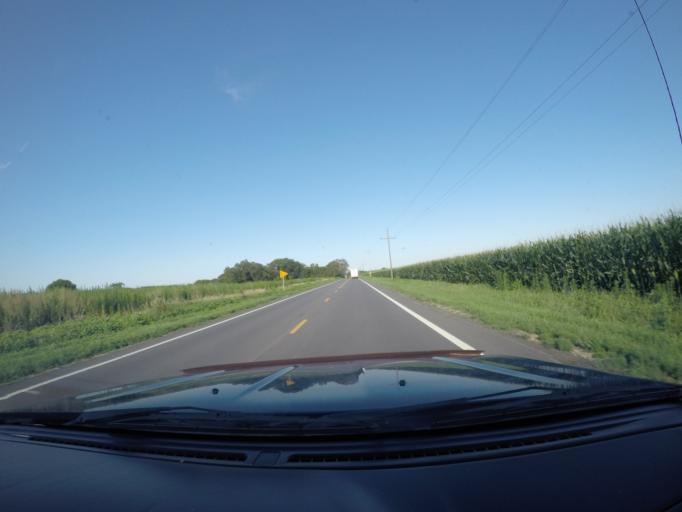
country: US
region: Kansas
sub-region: Douglas County
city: Lawrence
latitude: 39.0006
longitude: -95.2037
